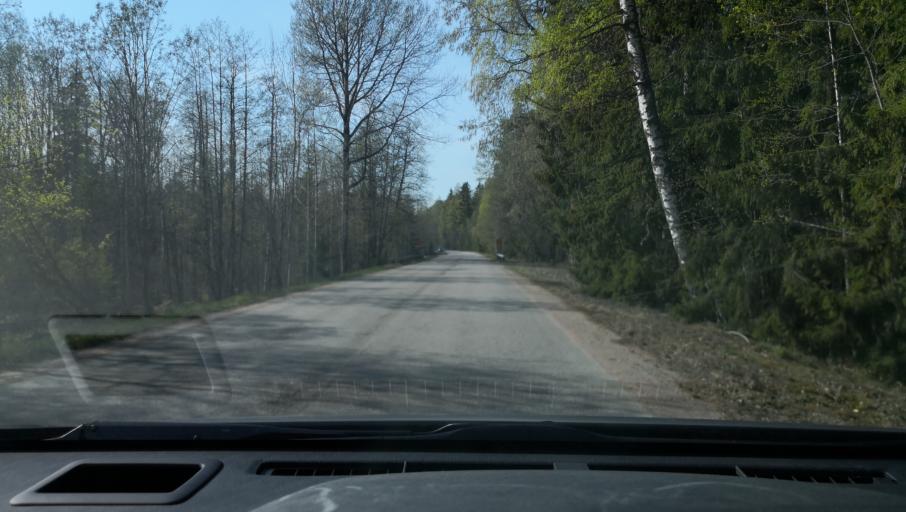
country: SE
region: Uppsala
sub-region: Heby Kommun
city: Tarnsjo
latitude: 60.2642
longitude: 16.9267
